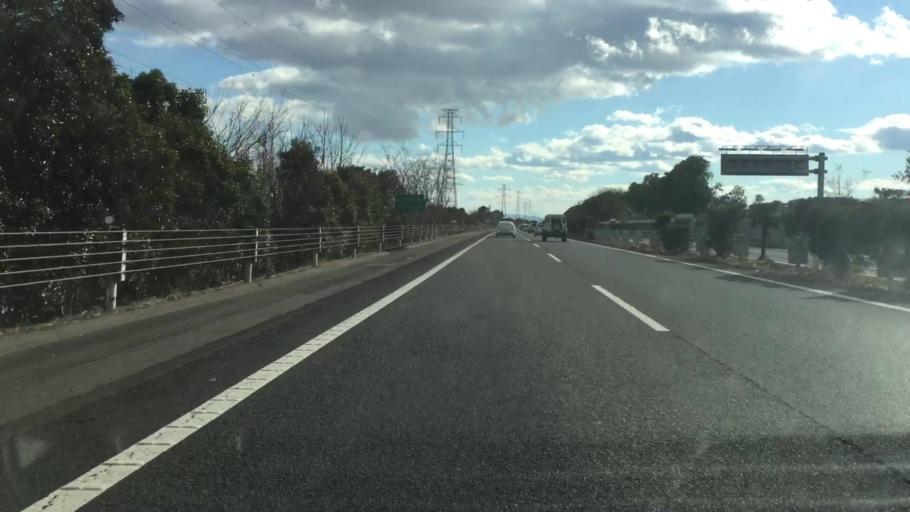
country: JP
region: Gunma
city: Shibukawa
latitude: 36.4573
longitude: 139.0132
